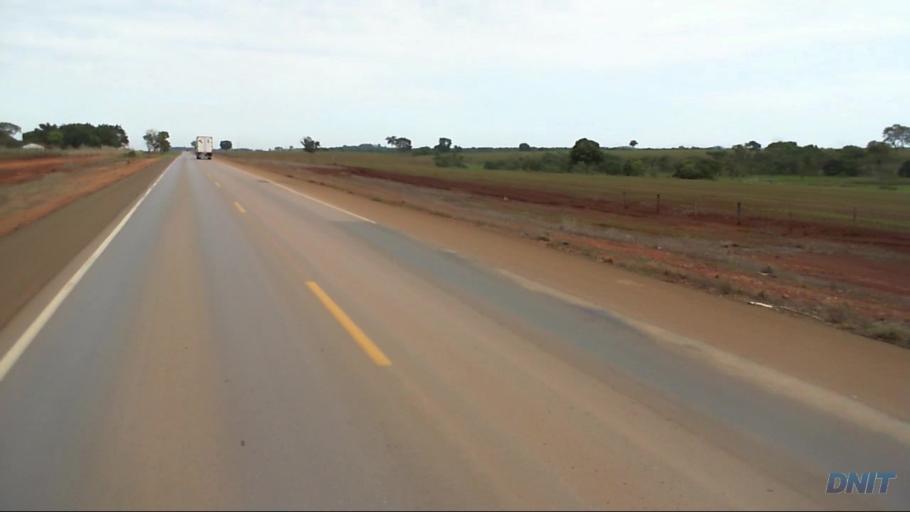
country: BR
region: Goias
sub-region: Uruacu
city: Uruacu
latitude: -14.7051
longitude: -49.1143
